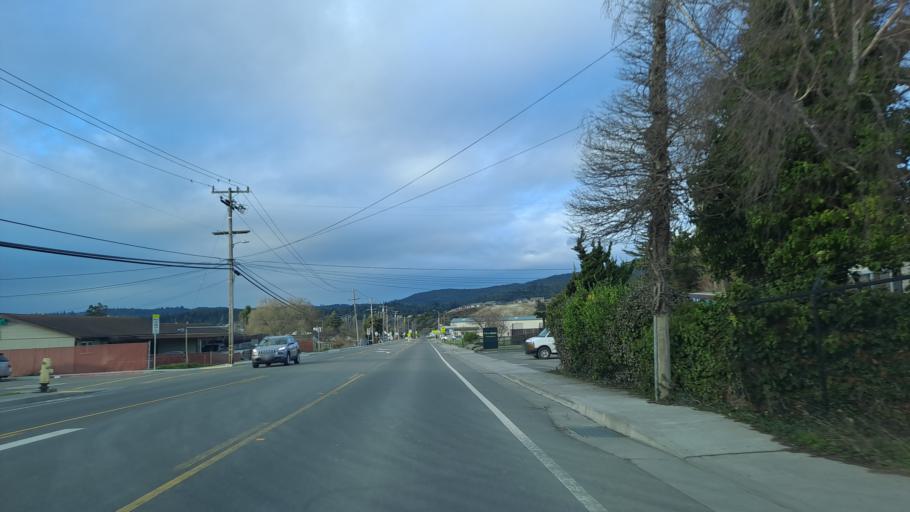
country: US
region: California
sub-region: Humboldt County
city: Fortuna
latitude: 40.5799
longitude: -124.1302
